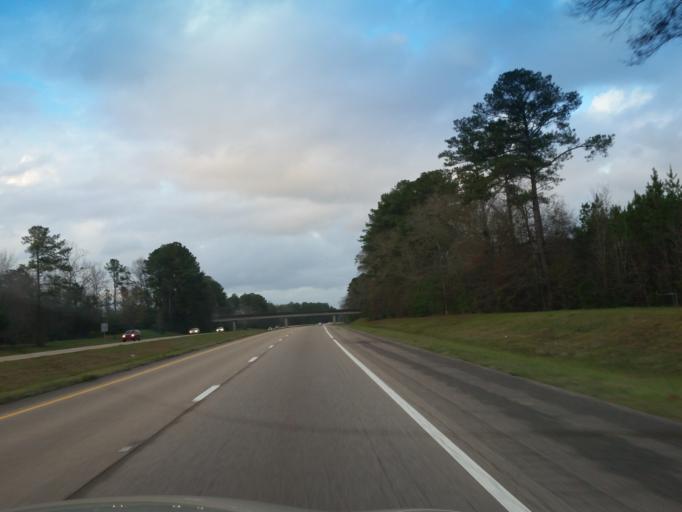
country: US
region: Mississippi
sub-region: Clarke County
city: Stonewall
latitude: 32.0357
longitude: -88.9214
